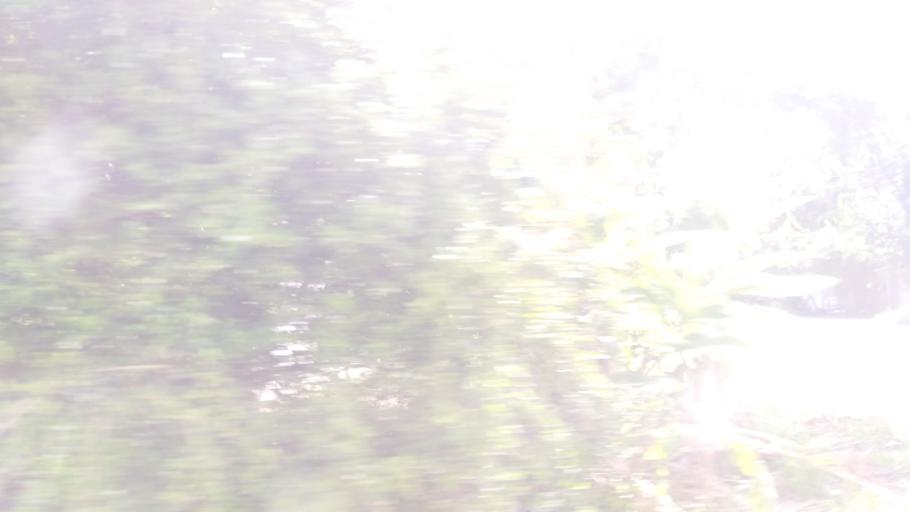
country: TH
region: Chaiyaphum
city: Ban Thaen
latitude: 16.4070
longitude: 102.3430
